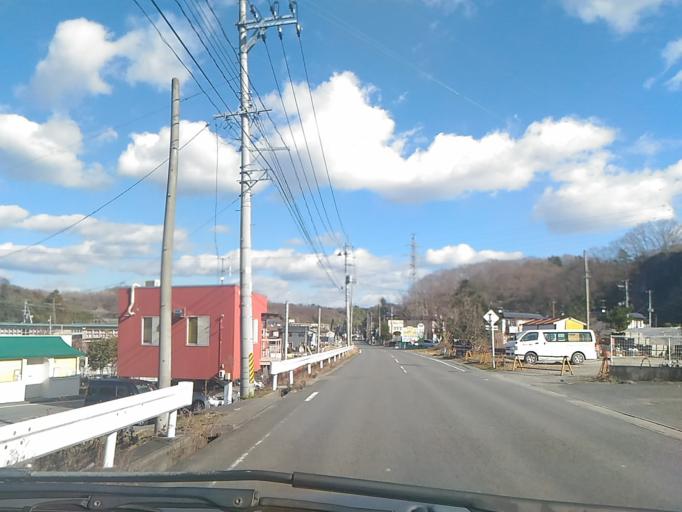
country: JP
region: Fukushima
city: Iwaki
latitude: 37.0138
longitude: 140.8374
